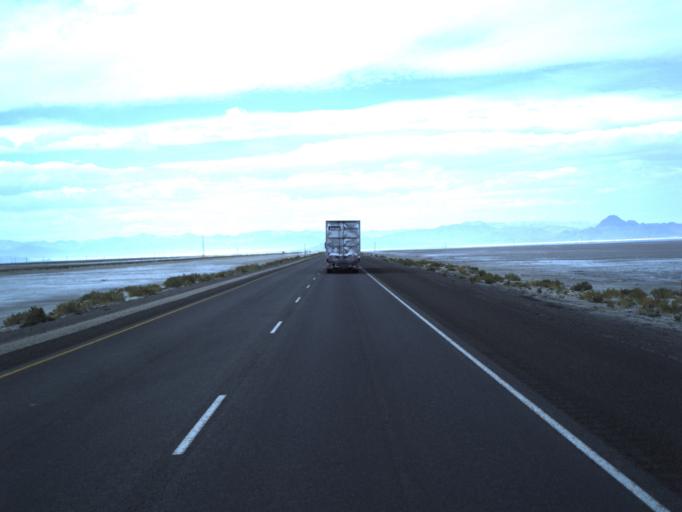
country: US
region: Utah
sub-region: Tooele County
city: Wendover
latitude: 40.7373
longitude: -113.7486
